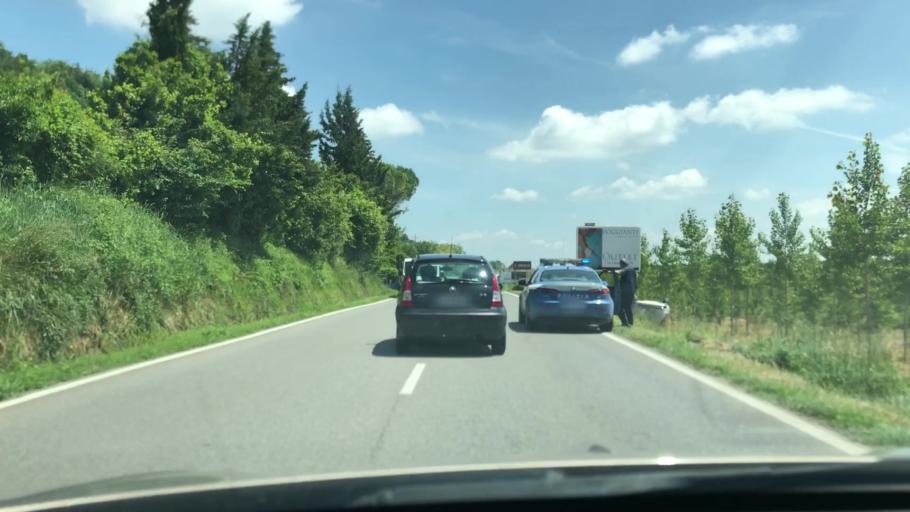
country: IT
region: Tuscany
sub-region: Province of Pisa
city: Treggiaia
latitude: 43.6122
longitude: 10.6848
